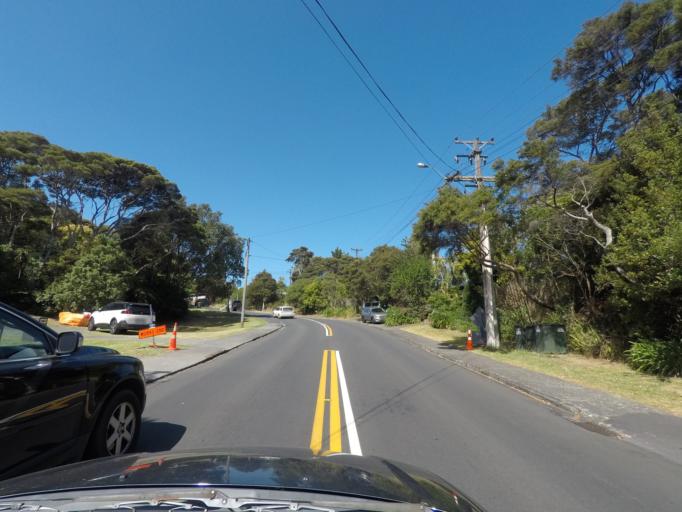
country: NZ
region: Auckland
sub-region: Auckland
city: Waitakere
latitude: -36.9231
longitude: 174.6567
